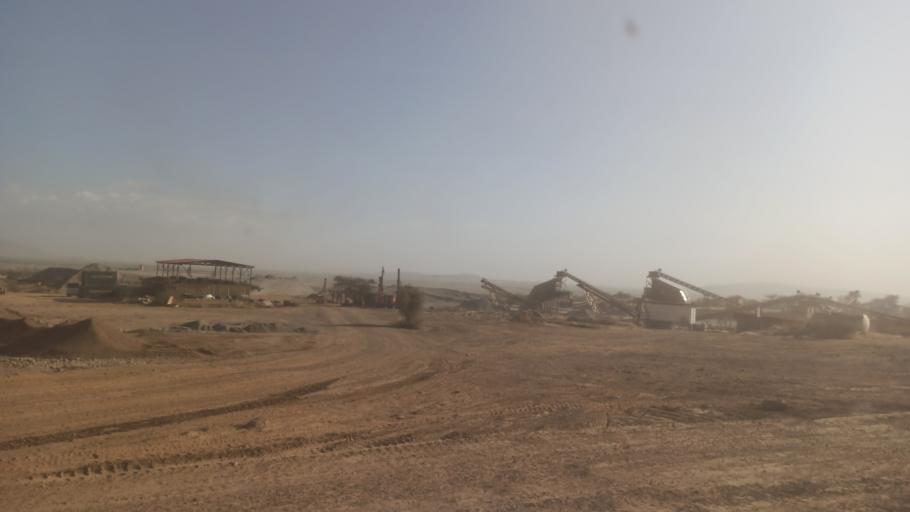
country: ET
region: Oromiya
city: Ziway
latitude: 7.9364
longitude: 38.6142
